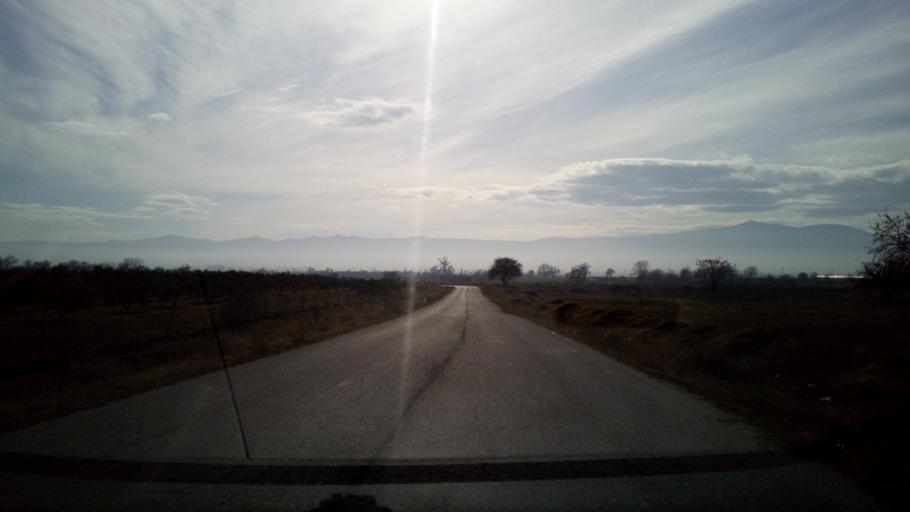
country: GR
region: Central Macedonia
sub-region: Nomos Thessalonikis
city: Gerakarou
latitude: 40.6832
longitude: 23.2474
